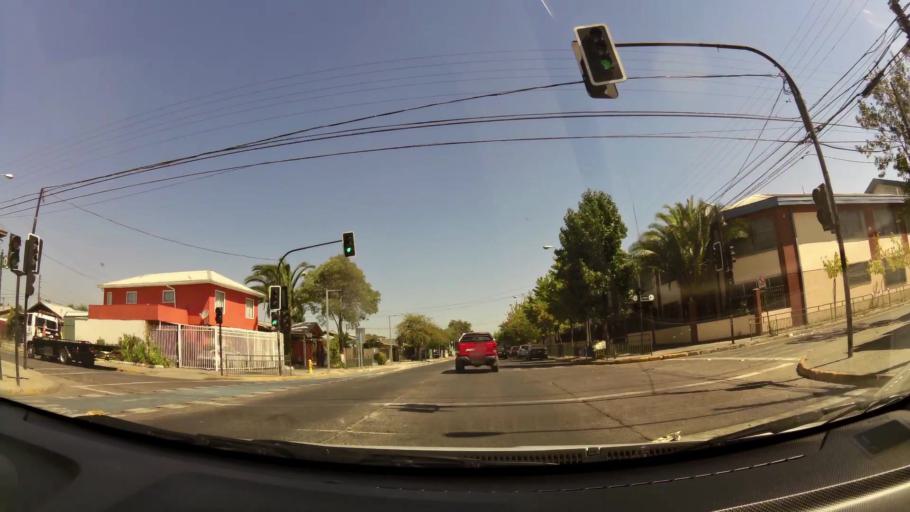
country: CL
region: Maule
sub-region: Provincia de Talca
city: Talca
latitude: -35.4190
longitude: -71.6493
